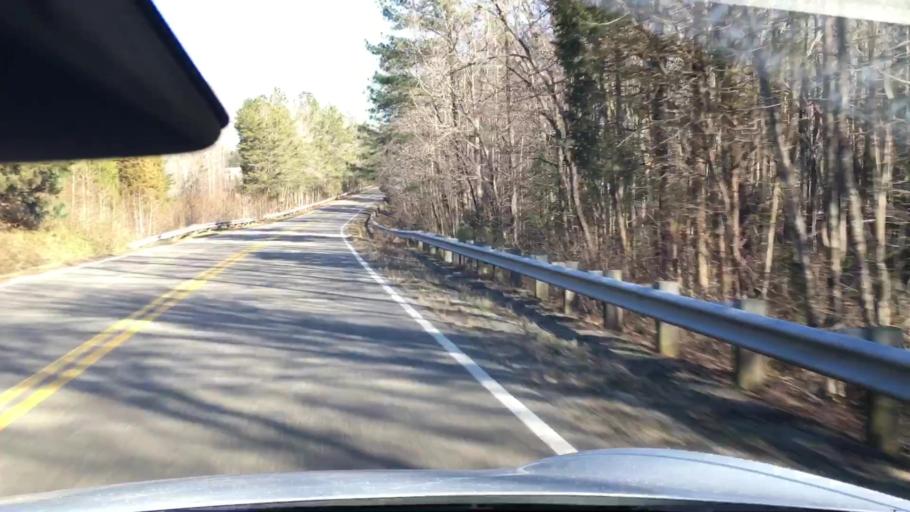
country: US
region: Virginia
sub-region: Powhatan County
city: Powhatan
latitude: 37.5308
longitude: -77.8010
